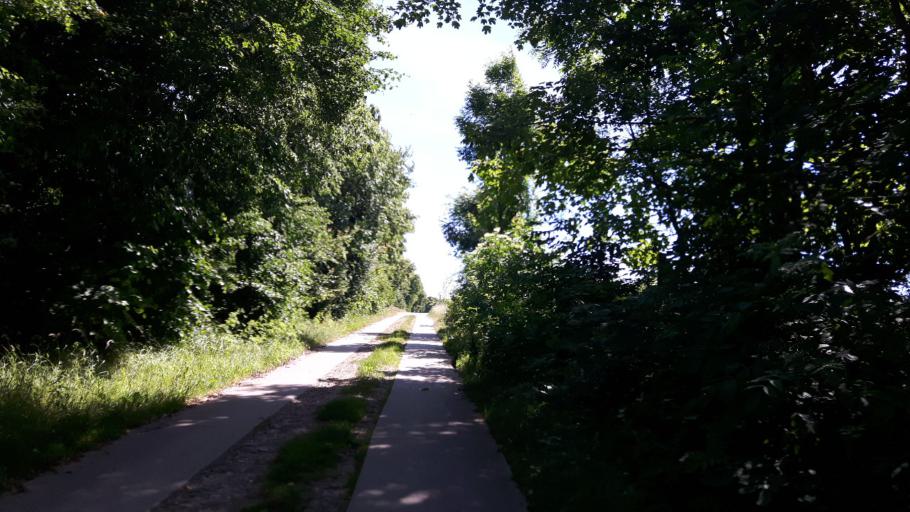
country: DE
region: Saxony-Anhalt
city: Grosskorbetha
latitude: 51.2321
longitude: 12.0444
